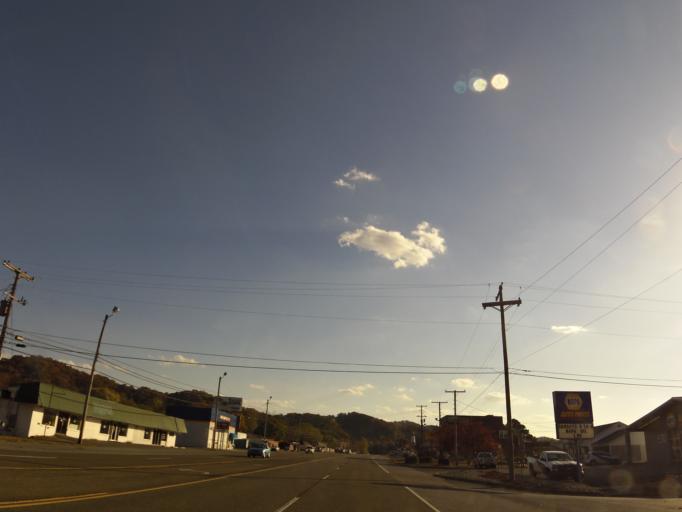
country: US
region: Tennessee
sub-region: Anderson County
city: Clinton
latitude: 36.0778
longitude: -84.1321
